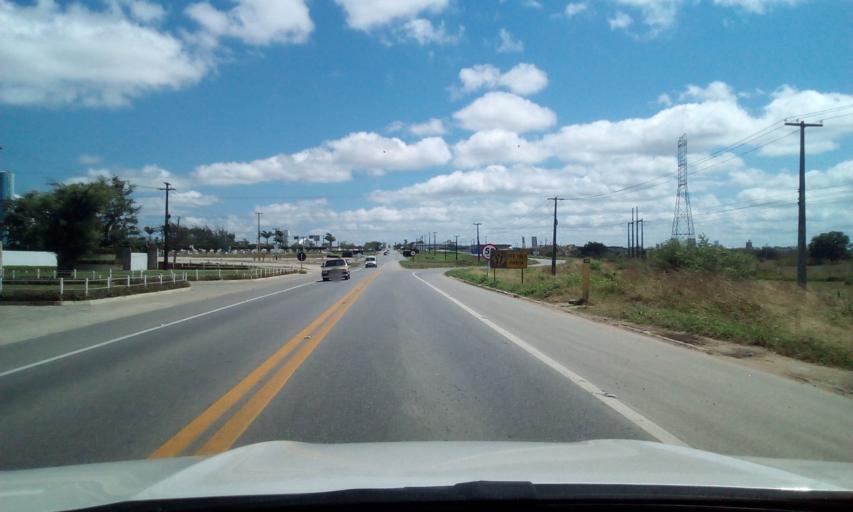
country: BR
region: Paraiba
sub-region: Campina Grande
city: Campina Grande
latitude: -7.2803
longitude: -35.8891
